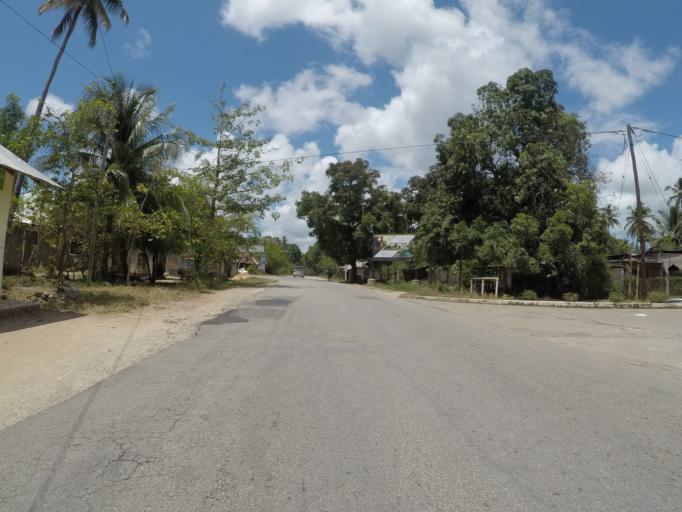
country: TZ
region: Zanzibar Central/South
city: Nganane
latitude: -6.2883
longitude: 39.4381
